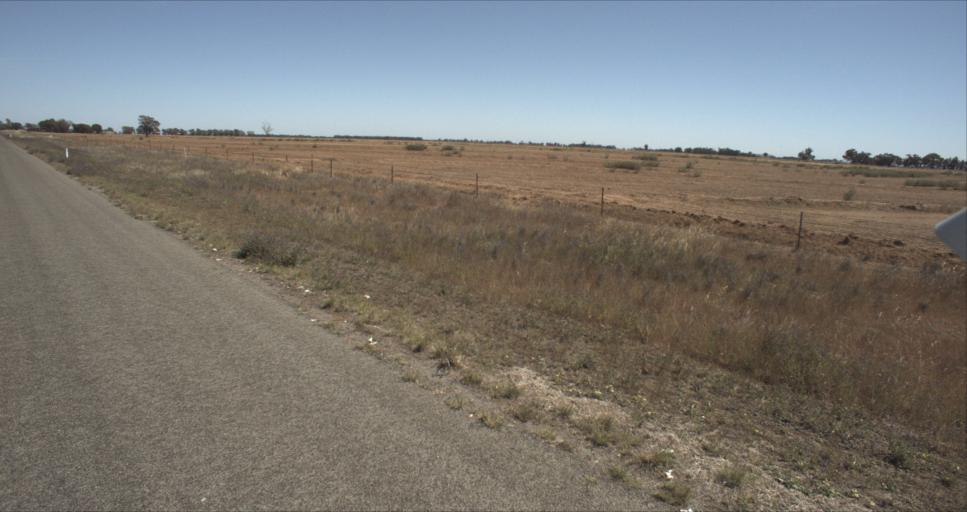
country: AU
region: New South Wales
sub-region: Leeton
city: Leeton
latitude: -34.5816
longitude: 146.2938
